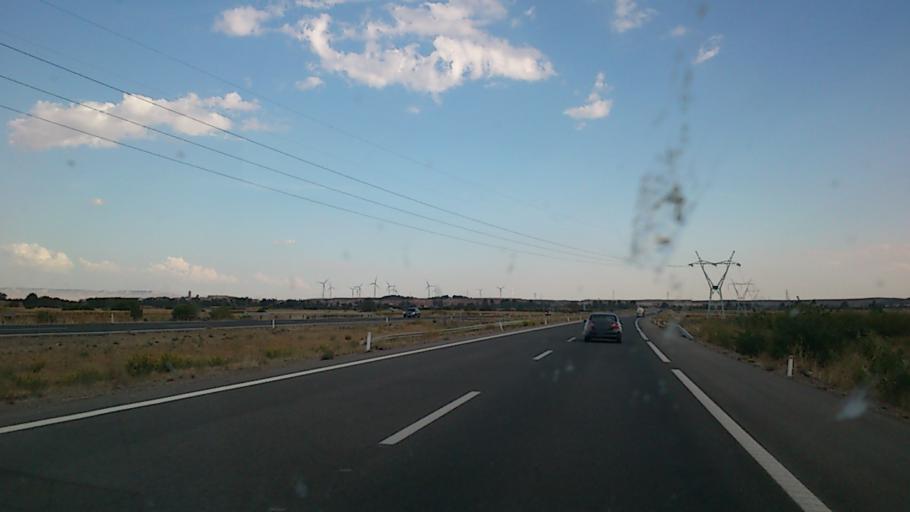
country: ES
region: Aragon
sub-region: Provincia de Zaragoza
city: Frescano
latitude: 41.9059
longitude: -1.4516
